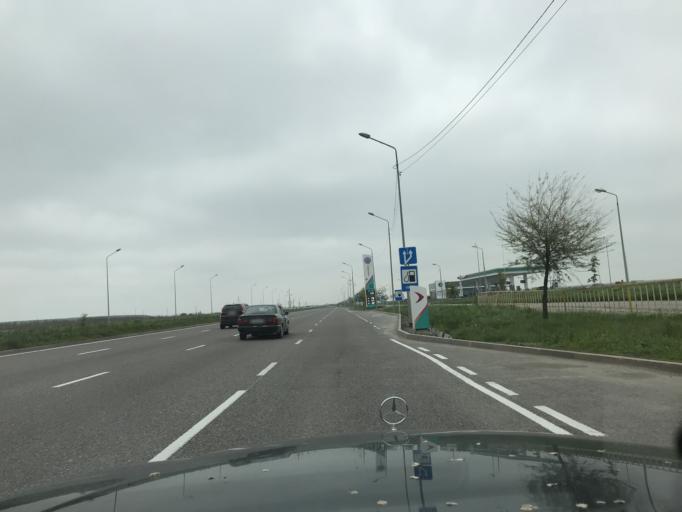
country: KZ
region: Almaty Oblysy
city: Burunday
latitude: 43.2944
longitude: 76.8317
